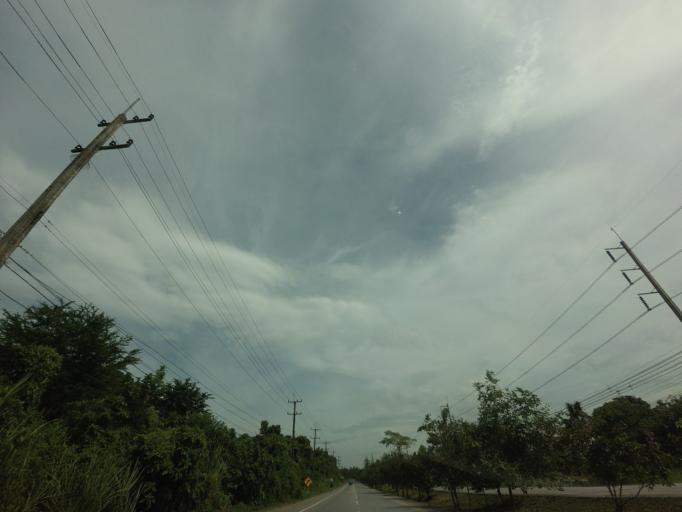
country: TH
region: Rayong
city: Klaeng
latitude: 12.6973
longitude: 101.5399
